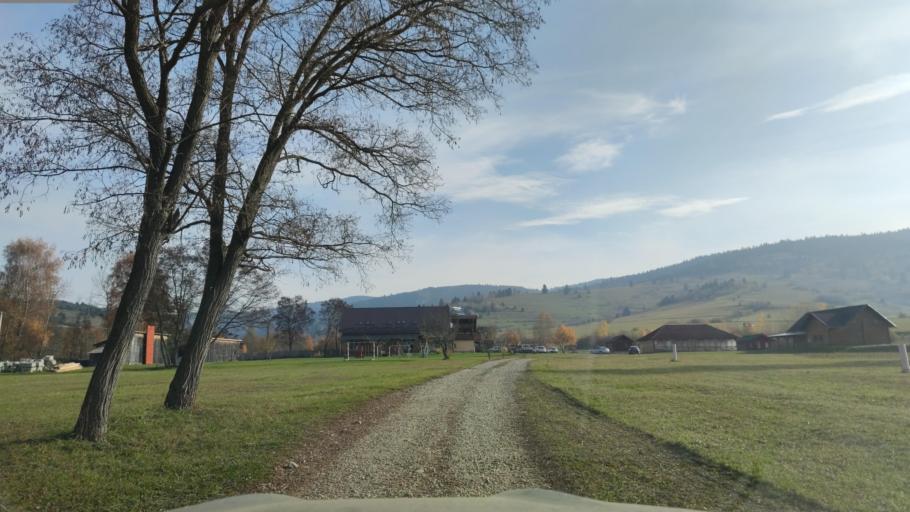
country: RO
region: Harghita
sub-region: Comuna Ditrau
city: Ditrau
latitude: 46.8213
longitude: 25.5394
